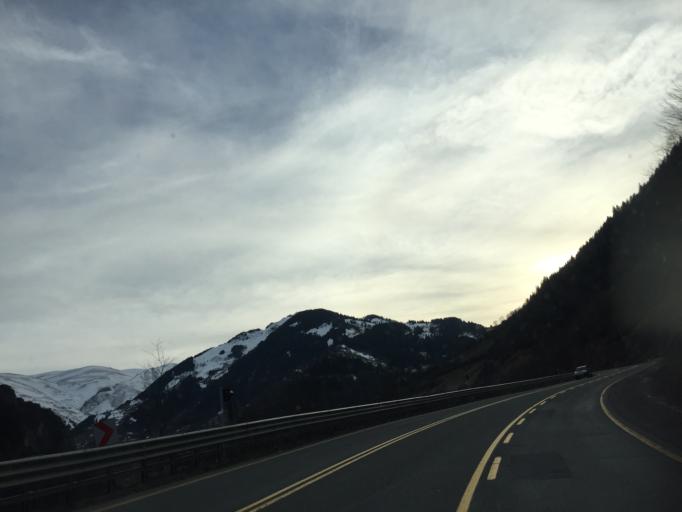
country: TR
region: Trabzon
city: Macka
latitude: 40.7049
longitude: 39.4917
